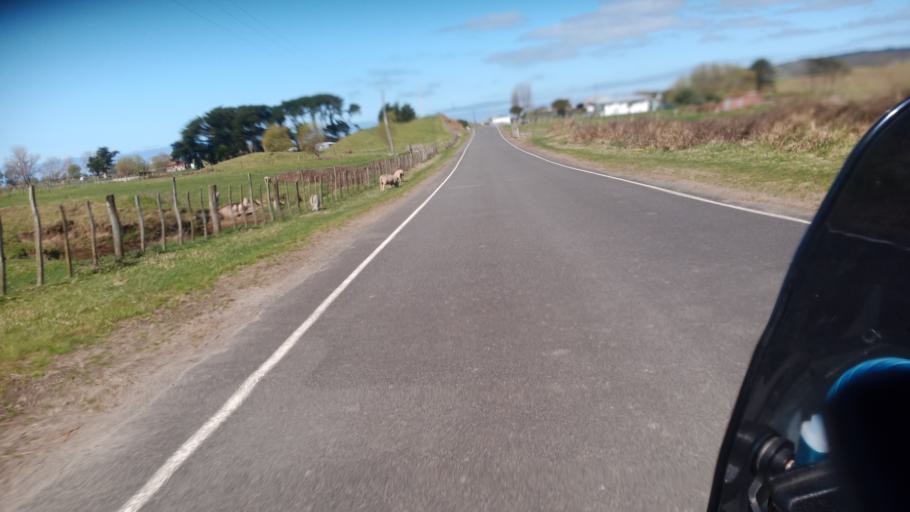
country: NZ
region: Gisborne
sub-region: Gisborne District
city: Gisborne
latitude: -39.0482
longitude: 177.8675
